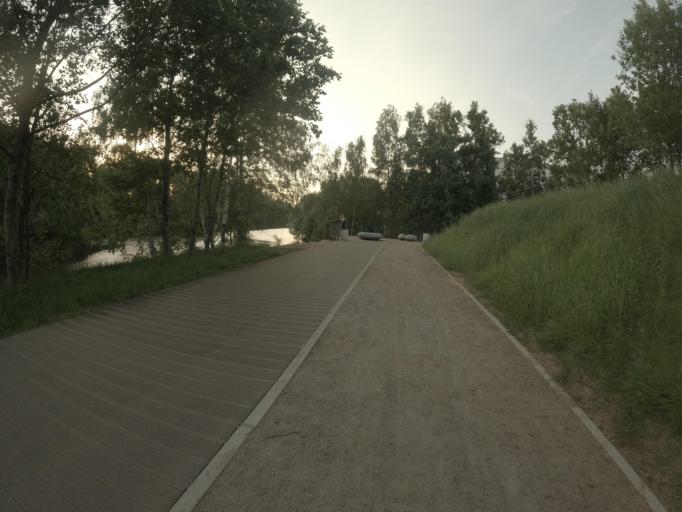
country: RU
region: St.-Petersburg
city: Krasnogvargeisky
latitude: 59.9453
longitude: 30.4570
